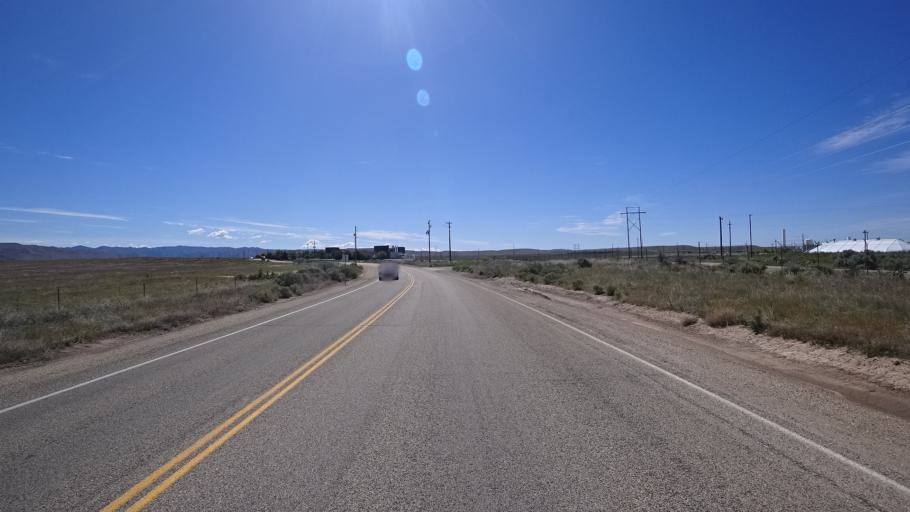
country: US
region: Idaho
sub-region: Ada County
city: Boise
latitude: 43.5317
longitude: -116.1401
